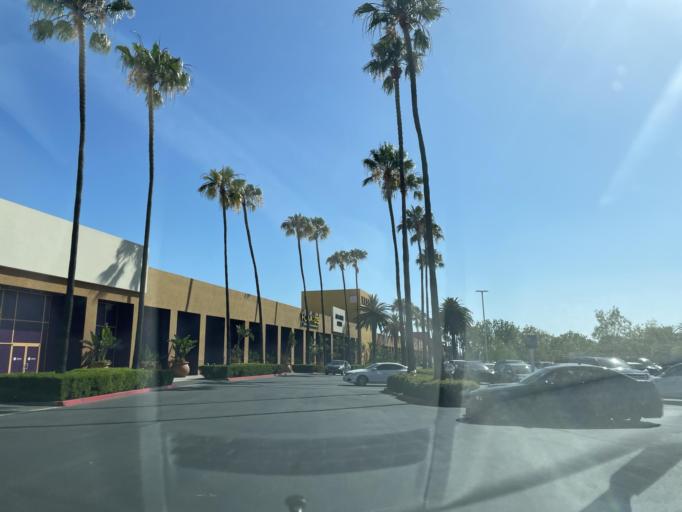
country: US
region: California
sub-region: Orange County
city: North Tustin
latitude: 33.7228
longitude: -117.7878
